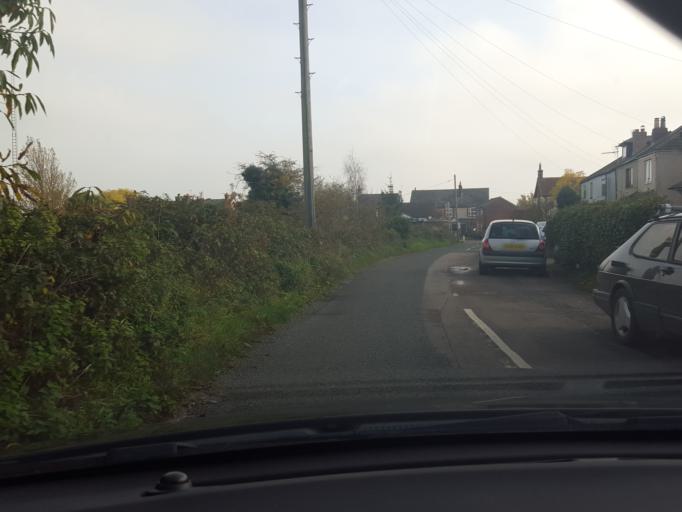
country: GB
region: England
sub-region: Essex
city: Mistley
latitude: 51.9392
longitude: 1.1704
